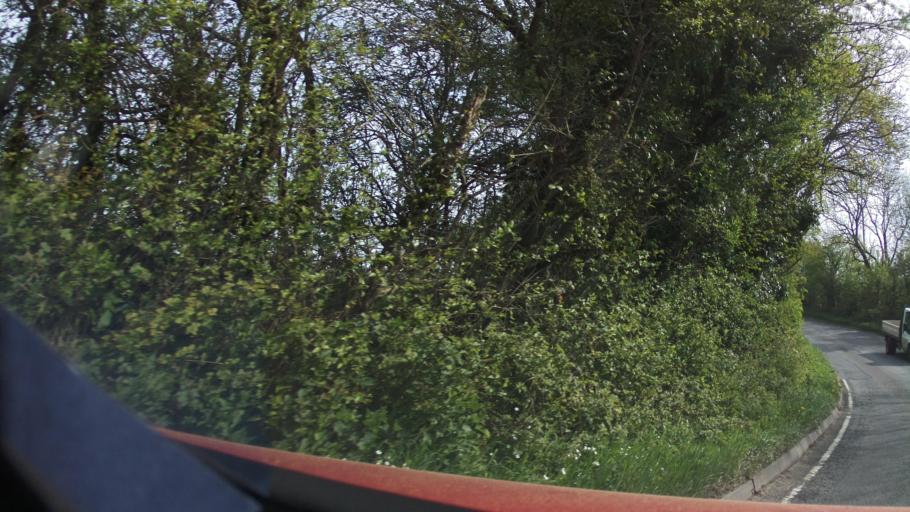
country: GB
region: England
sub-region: Somerset
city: Street
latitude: 51.1145
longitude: -2.7716
